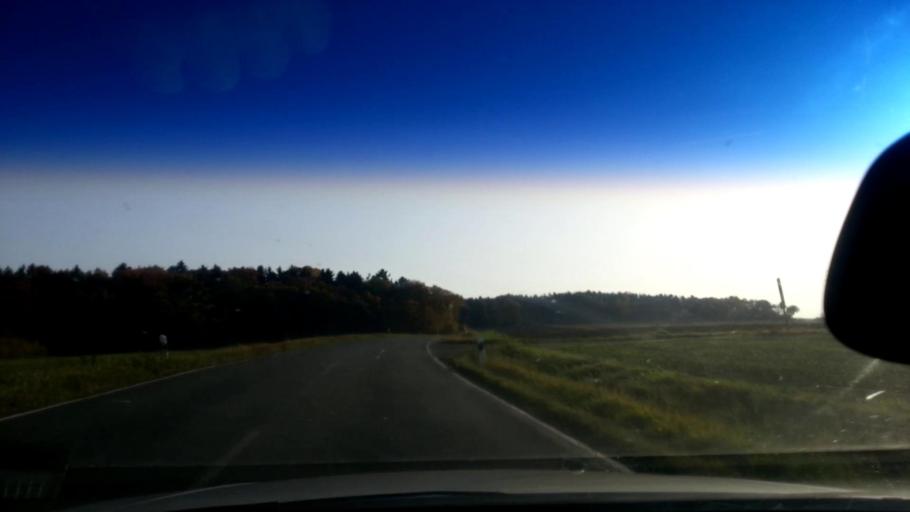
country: DE
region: Bavaria
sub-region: Upper Franconia
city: Poxdorf
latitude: 49.9715
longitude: 11.1130
